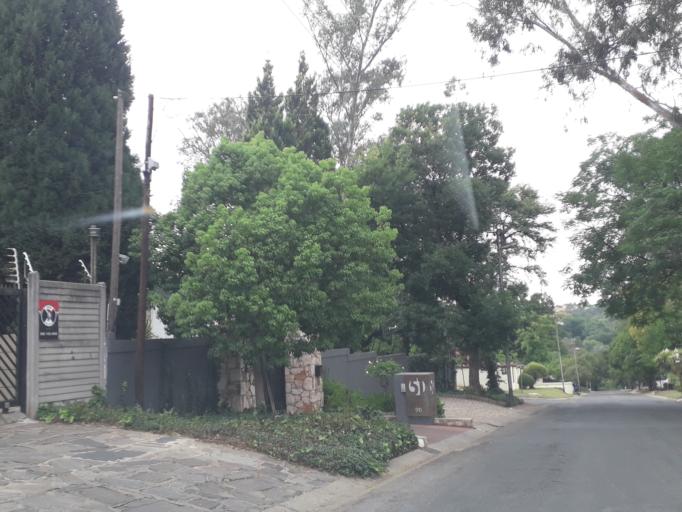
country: ZA
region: Gauteng
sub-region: City of Johannesburg Metropolitan Municipality
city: Midrand
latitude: -26.0402
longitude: 28.0493
